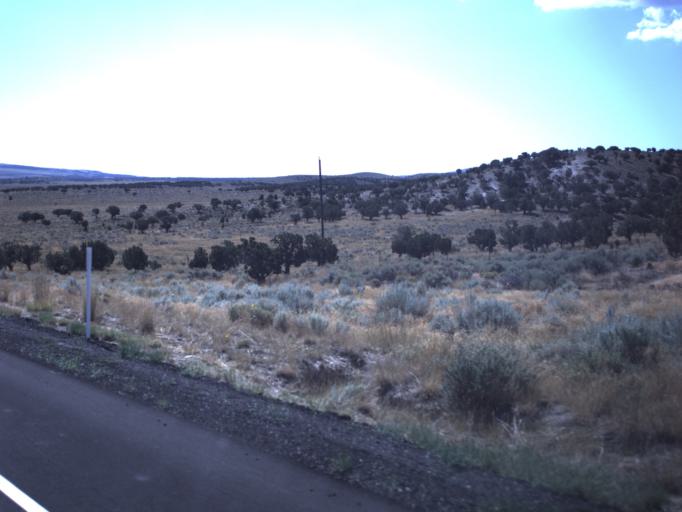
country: US
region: Utah
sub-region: Utah County
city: Eagle Mountain
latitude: 40.0675
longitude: -112.3258
